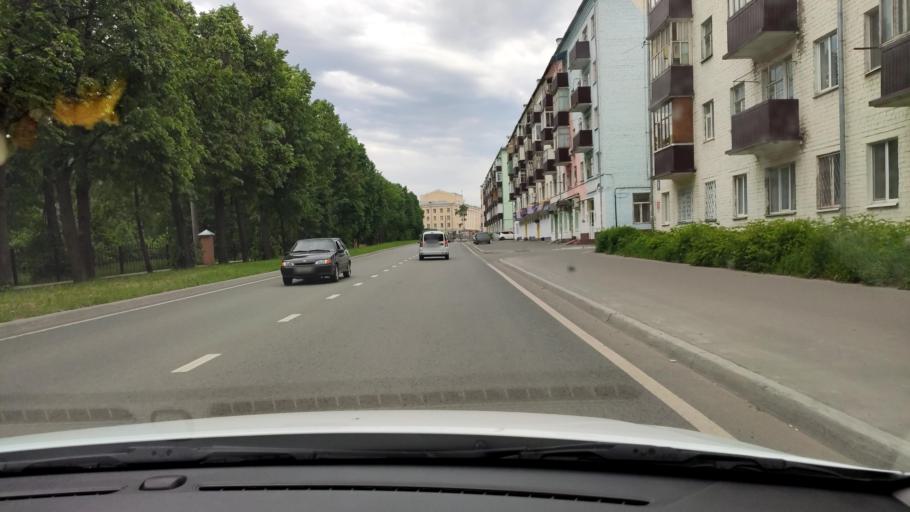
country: RU
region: Tatarstan
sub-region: Gorod Kazan'
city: Kazan
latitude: 55.8545
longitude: 49.0935
